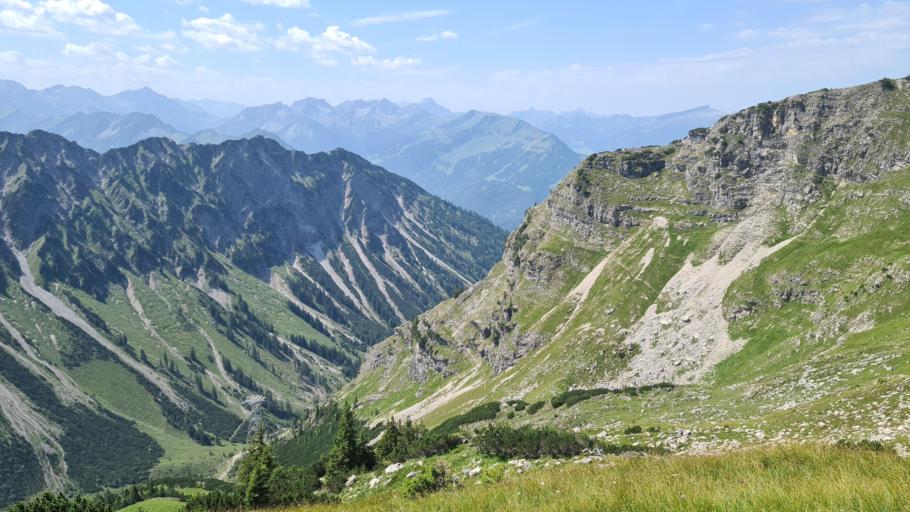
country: DE
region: Bavaria
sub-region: Swabia
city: Oberstdorf
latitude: 47.4166
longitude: 10.3338
